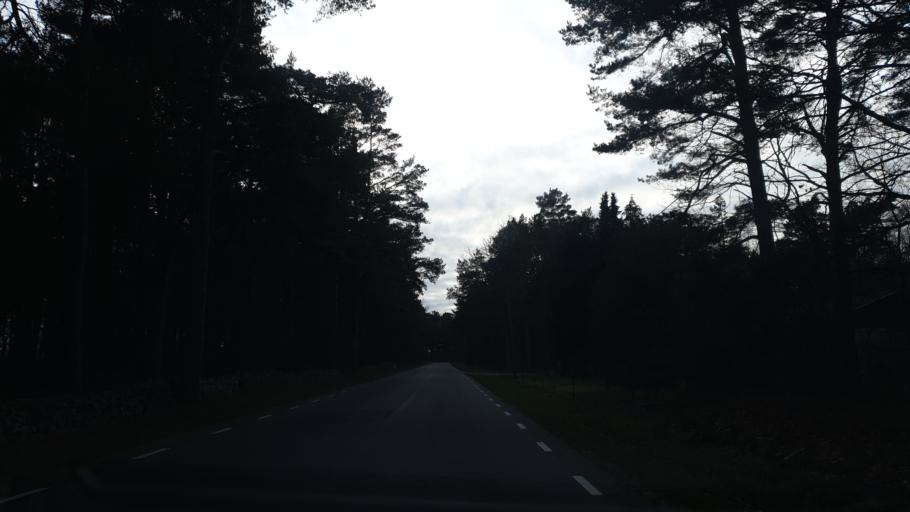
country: SE
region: Kalmar
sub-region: Torsas Kommun
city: Torsas
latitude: 56.2512
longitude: 16.0067
